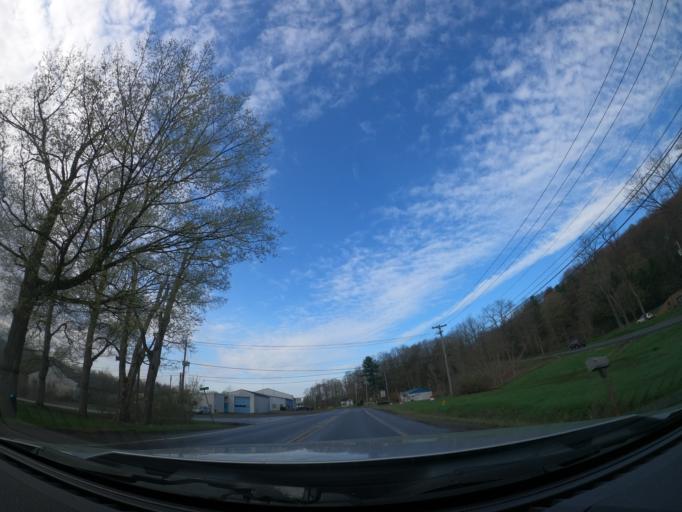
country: US
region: New York
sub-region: Cortland County
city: Homer
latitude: 42.6280
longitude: -76.1525
